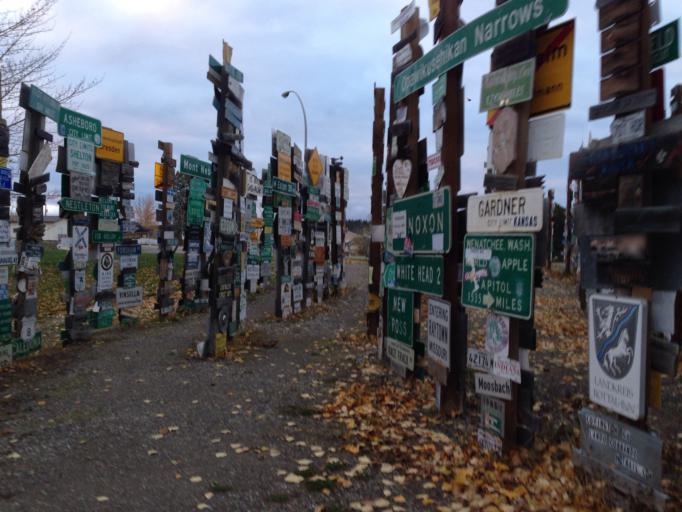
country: CA
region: Yukon
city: Watson Lake
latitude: 60.0634
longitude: -128.7152
